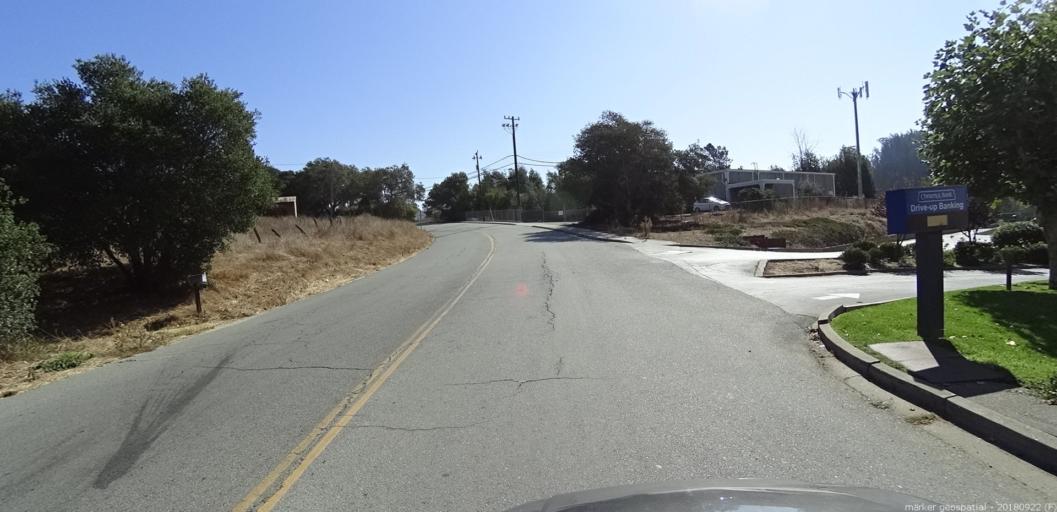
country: US
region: California
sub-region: Monterey County
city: Prunedale
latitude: 36.8028
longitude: -121.6659
